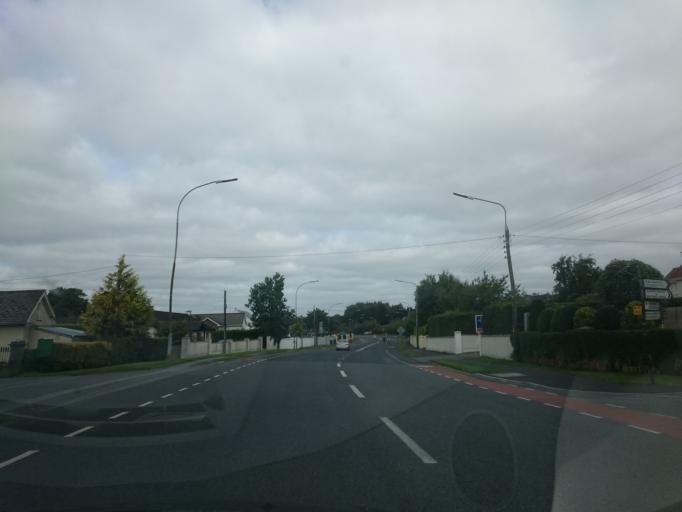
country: IE
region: Leinster
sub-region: Kilkenny
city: Kilkenny
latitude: 52.6676
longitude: -7.2527
